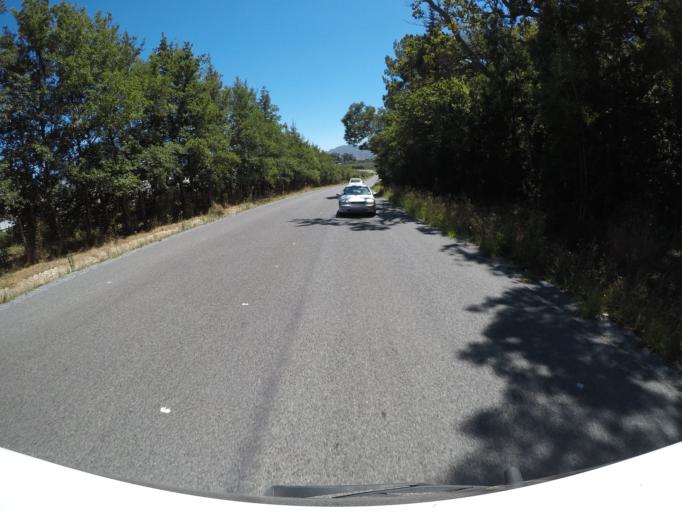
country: ZA
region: Western Cape
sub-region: Overberg District Municipality
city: Grabouw
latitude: -34.1716
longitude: 19.0347
